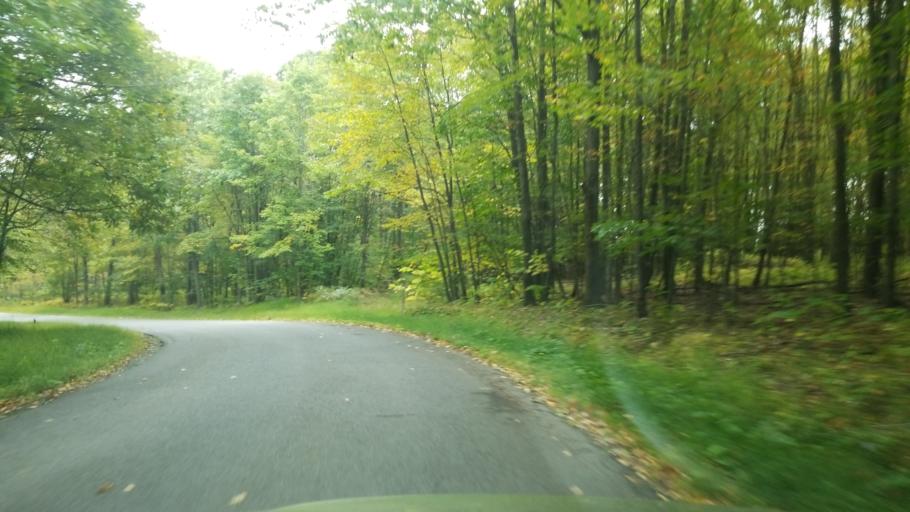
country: US
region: Pennsylvania
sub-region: Clearfield County
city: Curwensville
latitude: 41.0102
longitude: -78.5477
